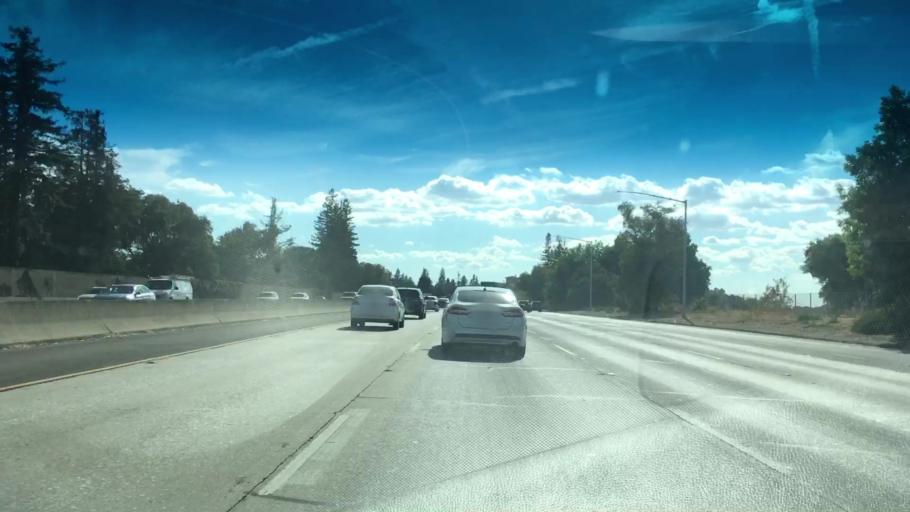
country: US
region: California
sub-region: Yolo County
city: West Sacramento
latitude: 38.5388
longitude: -121.5129
